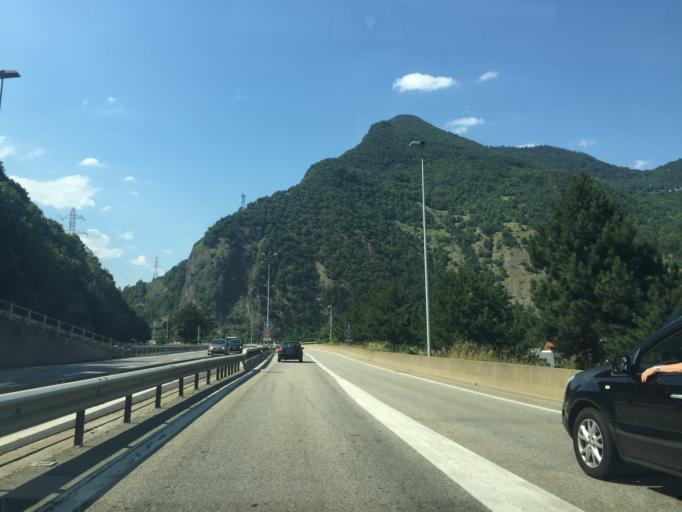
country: FR
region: Rhone-Alpes
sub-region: Departement de la Savoie
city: Moutiers
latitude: 45.4825
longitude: 6.5253
